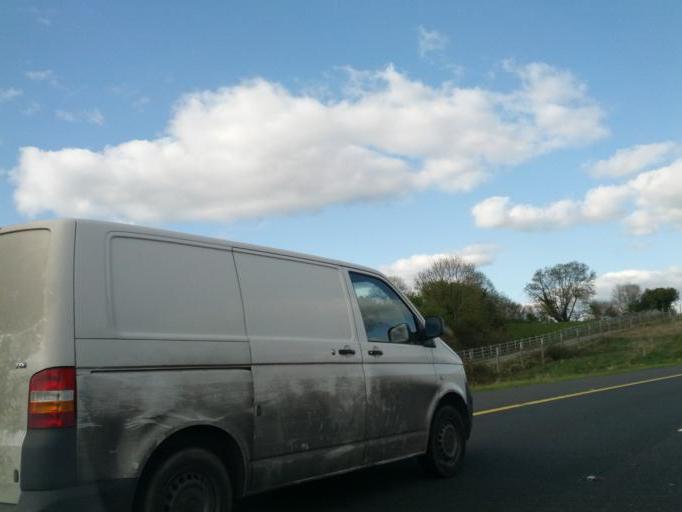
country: IE
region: Leinster
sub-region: An Iarmhi
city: Athlone
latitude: 53.4122
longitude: -8.0136
